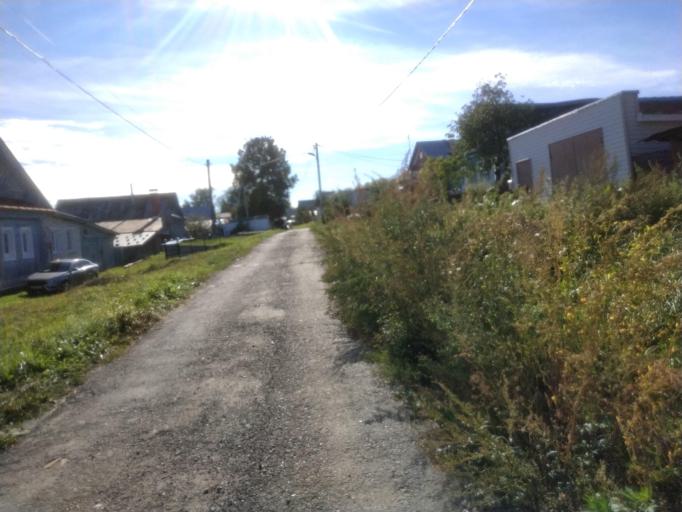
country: RU
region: Chuvashia
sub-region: Cheboksarskiy Rayon
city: Cheboksary
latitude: 56.1484
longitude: 47.1526
